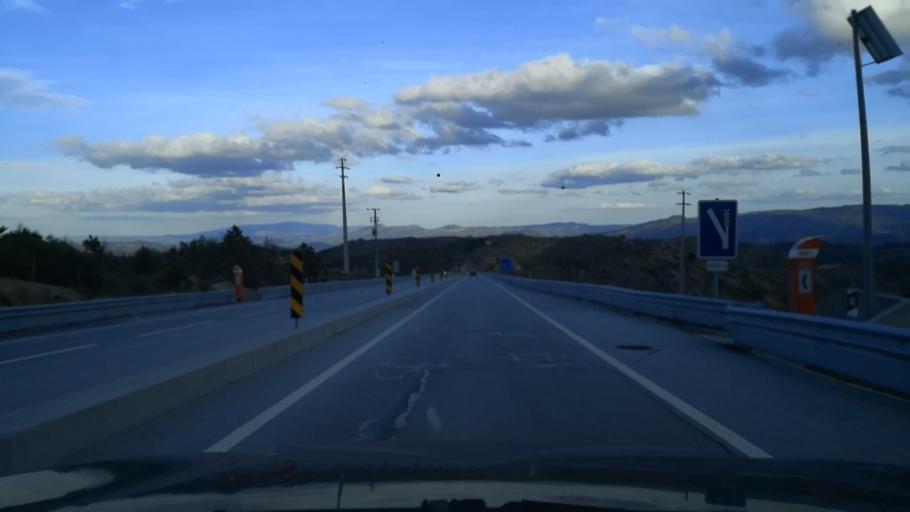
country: PT
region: Vila Real
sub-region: Murca
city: Murca
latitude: 41.3297
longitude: -7.4311
